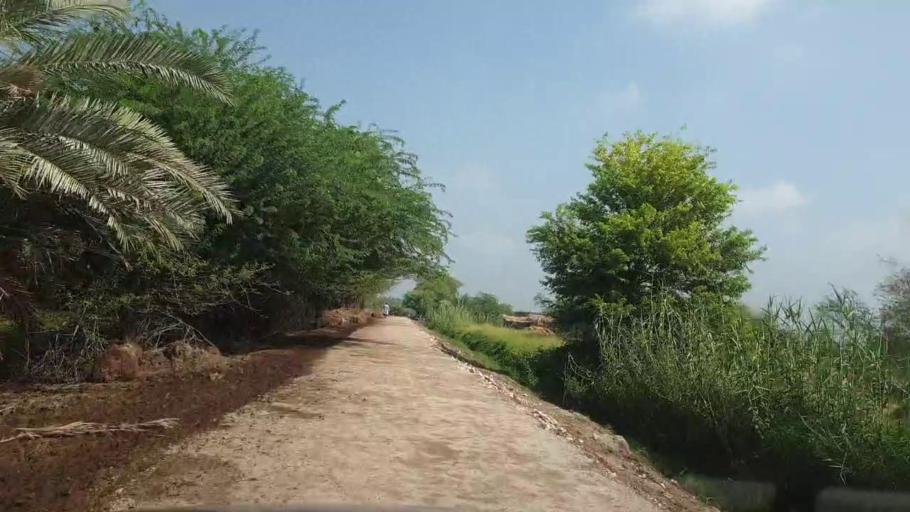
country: PK
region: Sindh
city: Pir jo Goth
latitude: 27.5978
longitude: 68.6938
